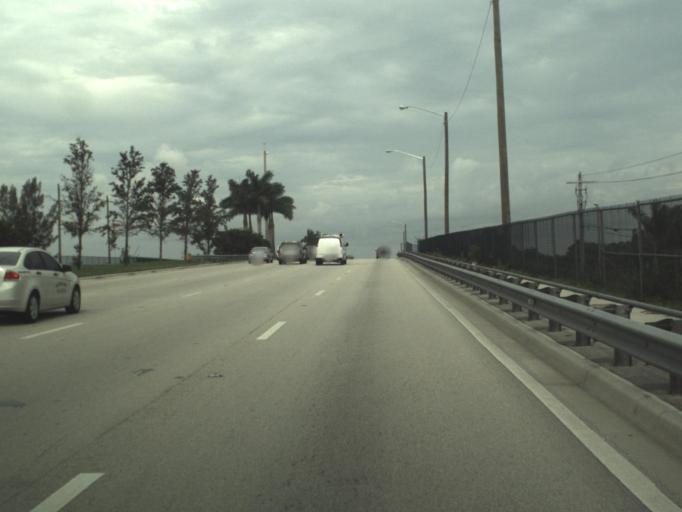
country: US
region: Florida
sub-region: Palm Beach County
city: Plantation Mobile Home Park
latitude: 26.7078
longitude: -80.1391
